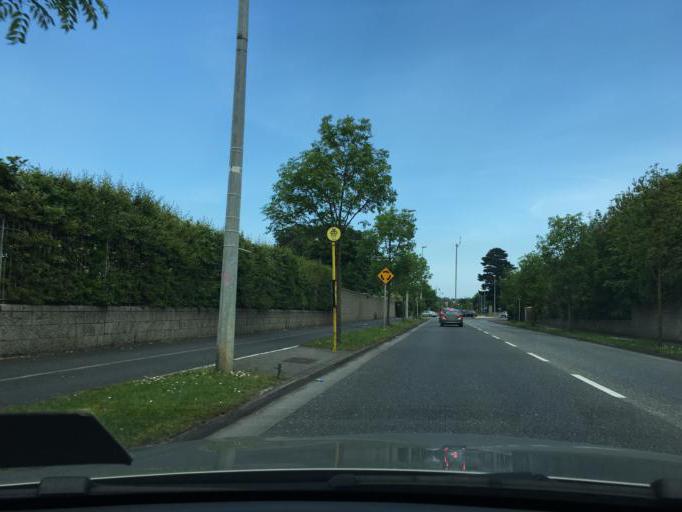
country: IE
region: Leinster
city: Templeogue
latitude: 53.2824
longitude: -6.2993
